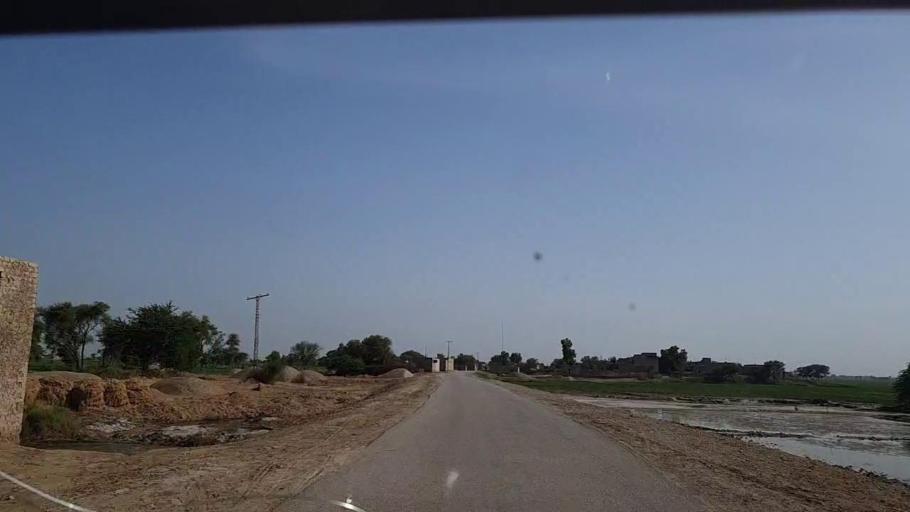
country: PK
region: Sindh
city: Khairpur Nathan Shah
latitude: 26.9988
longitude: 67.6666
